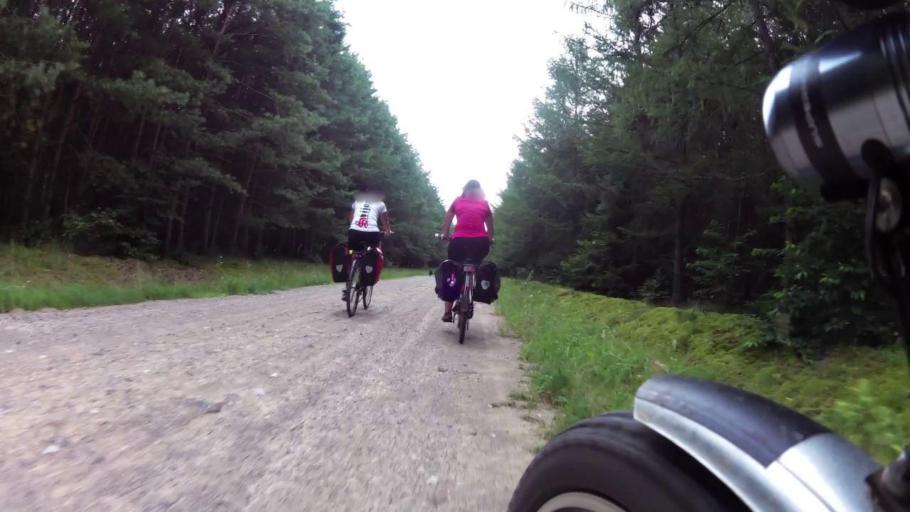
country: PL
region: West Pomeranian Voivodeship
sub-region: Powiat gryfinski
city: Mieszkowice
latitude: 52.8429
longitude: 14.5978
